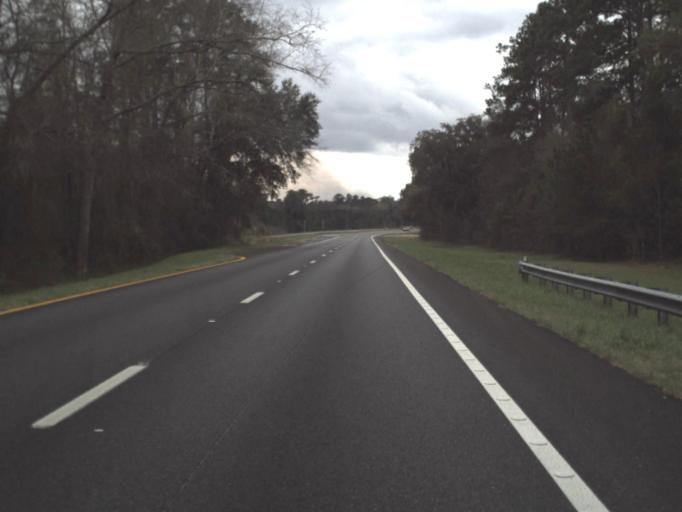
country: US
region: Florida
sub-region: Leon County
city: Tallahassee
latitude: 30.6267
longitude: -84.1698
